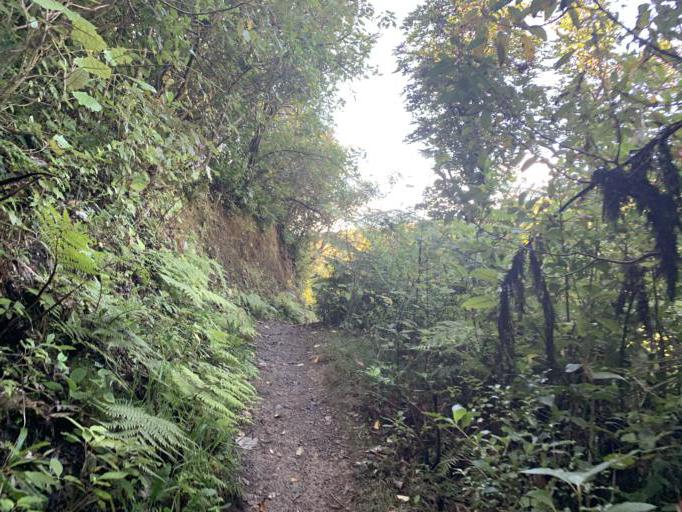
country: NZ
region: Wellington
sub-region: Wellington City
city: Brooklyn
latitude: -41.3002
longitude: 174.7536
